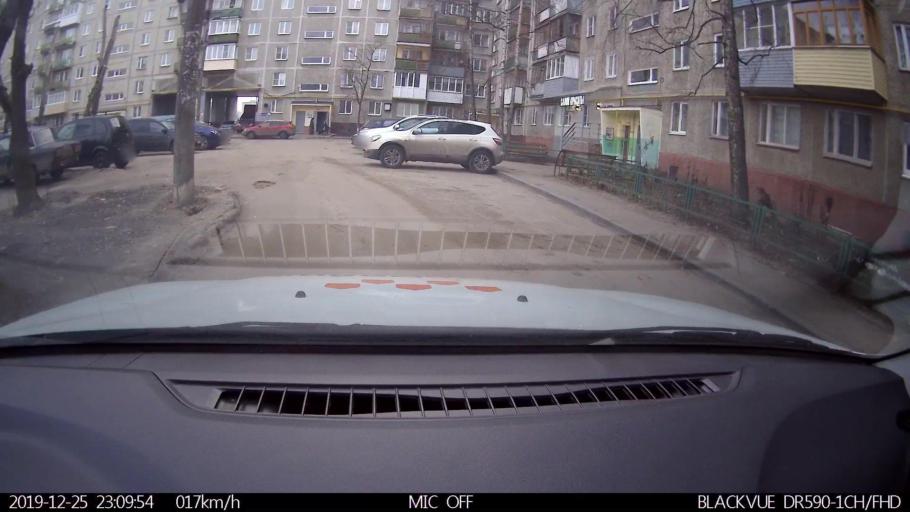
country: RU
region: Nizjnij Novgorod
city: Gorbatovka
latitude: 56.3609
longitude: 43.8226
